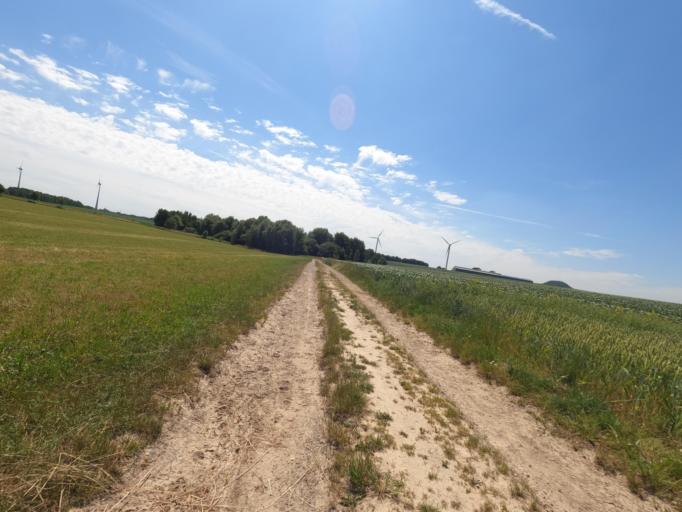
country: DE
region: North Rhine-Westphalia
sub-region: Regierungsbezirk Koln
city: Alsdorf
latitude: 50.9048
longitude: 6.1519
